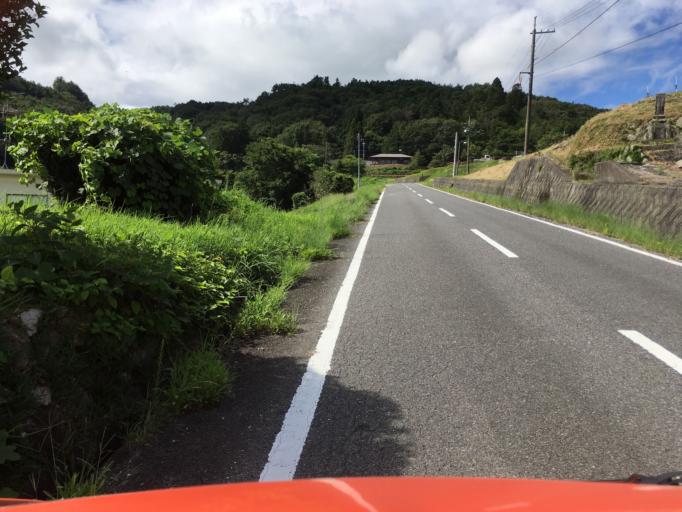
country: JP
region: Okayama
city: Tsuyama
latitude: 34.9011
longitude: 134.1317
